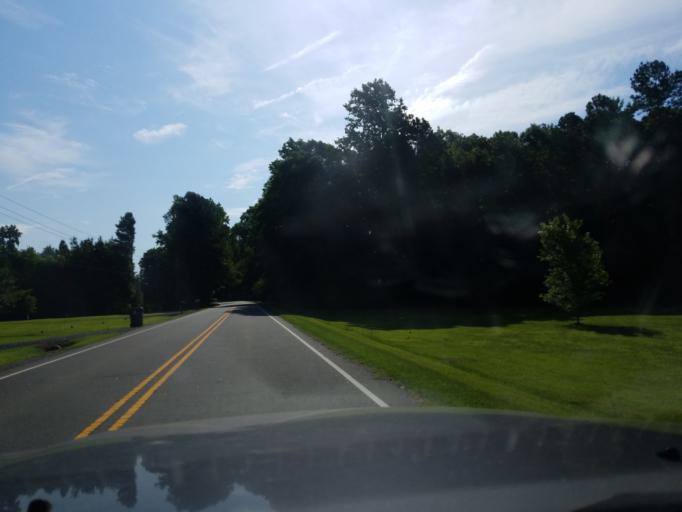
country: US
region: North Carolina
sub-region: Granville County
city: Butner
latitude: 36.2294
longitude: -78.7088
